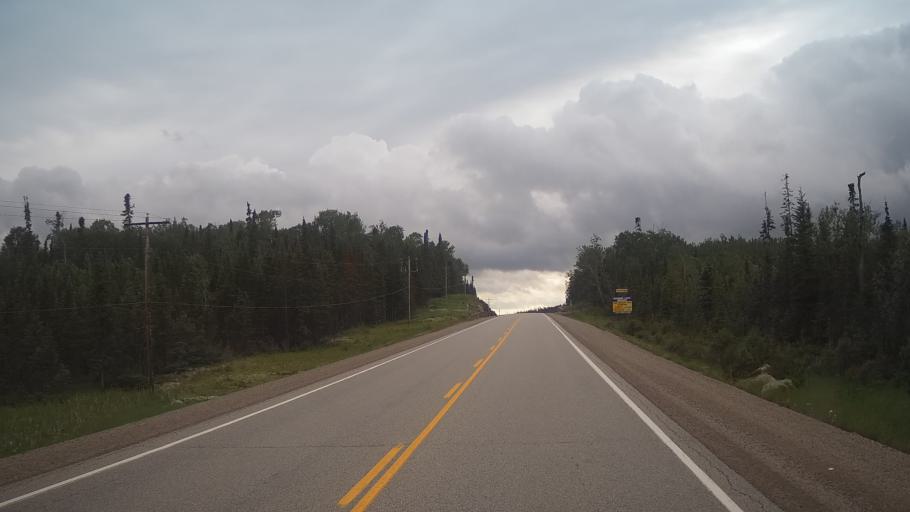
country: CA
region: Ontario
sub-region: Thunder Bay District
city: Thunder Bay
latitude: 48.9465
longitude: -90.1946
